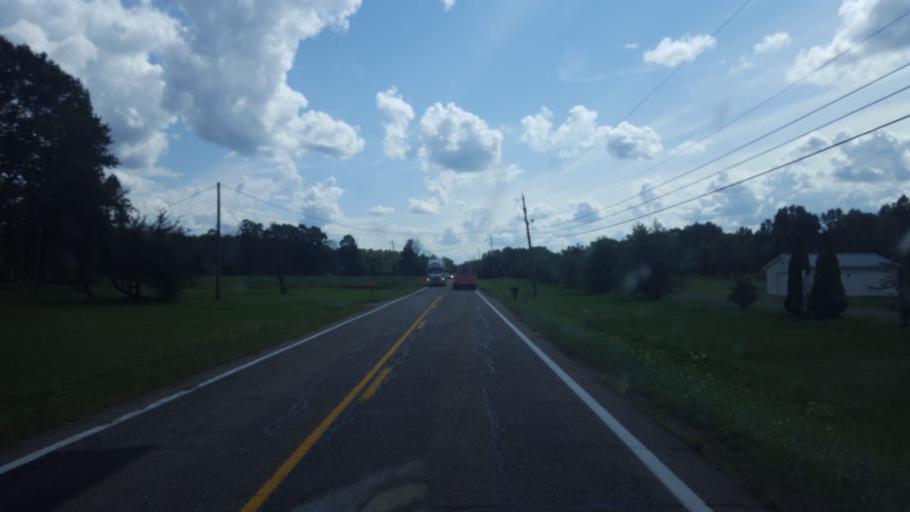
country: US
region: Ohio
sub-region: Portage County
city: Hiram
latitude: 41.2569
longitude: -81.1457
